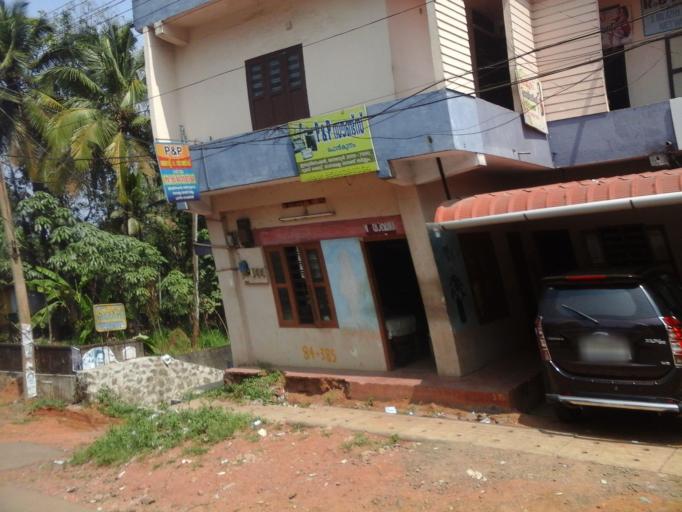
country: IN
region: Kerala
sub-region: Kottayam
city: Erattupetta
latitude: 9.5686
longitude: 76.7532
